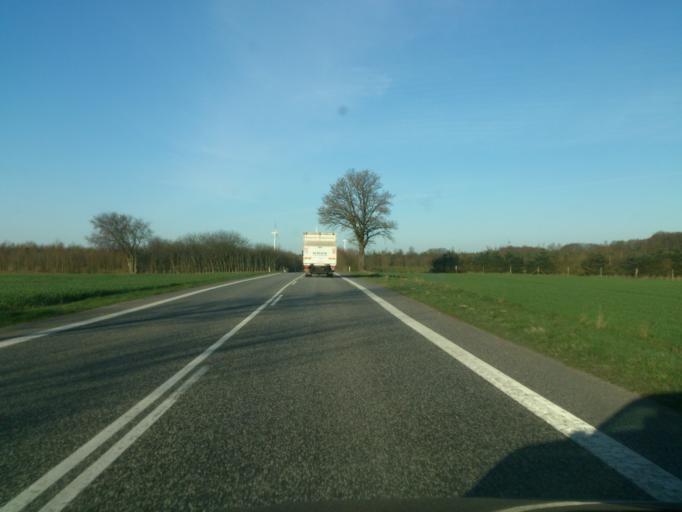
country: DK
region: Central Jutland
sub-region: Viborg Kommune
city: Bjerringbro
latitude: 56.4386
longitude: 9.6940
